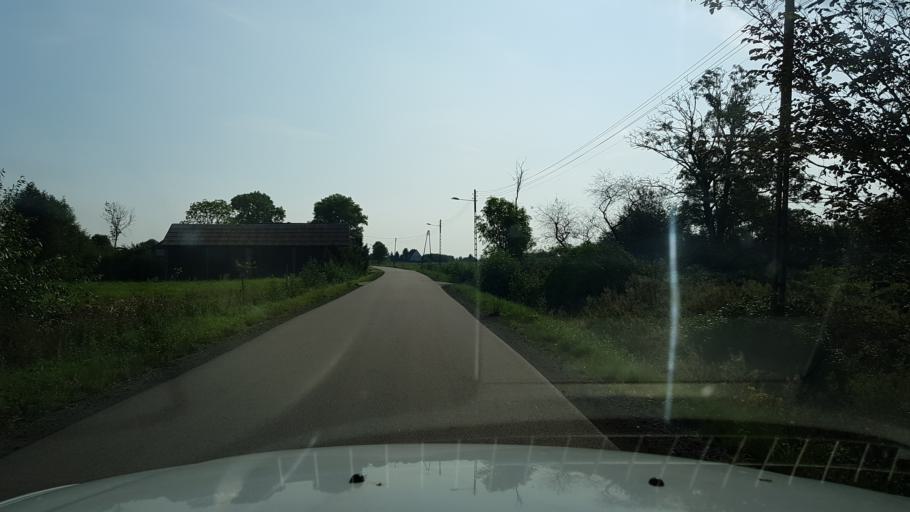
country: PL
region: West Pomeranian Voivodeship
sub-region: Powiat slawienski
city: Slawno
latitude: 54.3743
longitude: 16.5995
